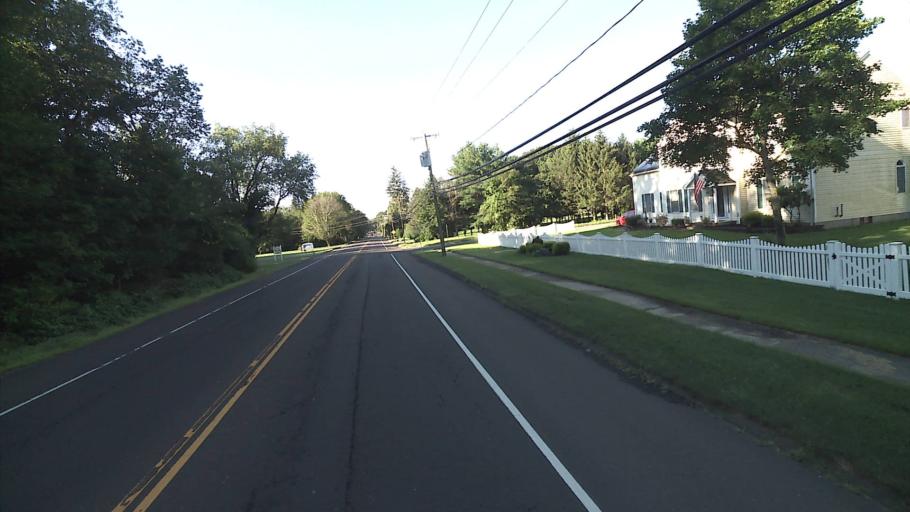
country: US
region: Connecticut
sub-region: New Haven County
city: Cheshire
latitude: 41.4633
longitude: -72.9075
